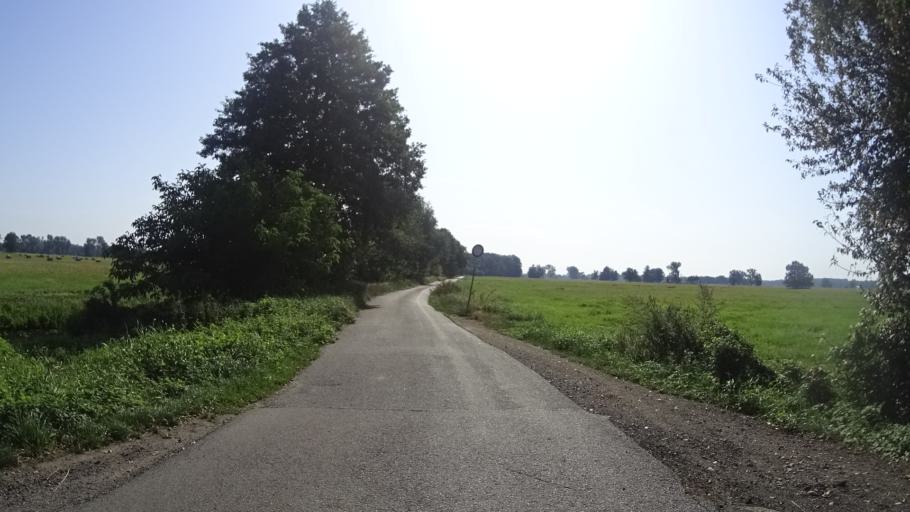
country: DE
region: Brandenburg
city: Neu Zauche
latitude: 51.9059
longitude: 14.0711
